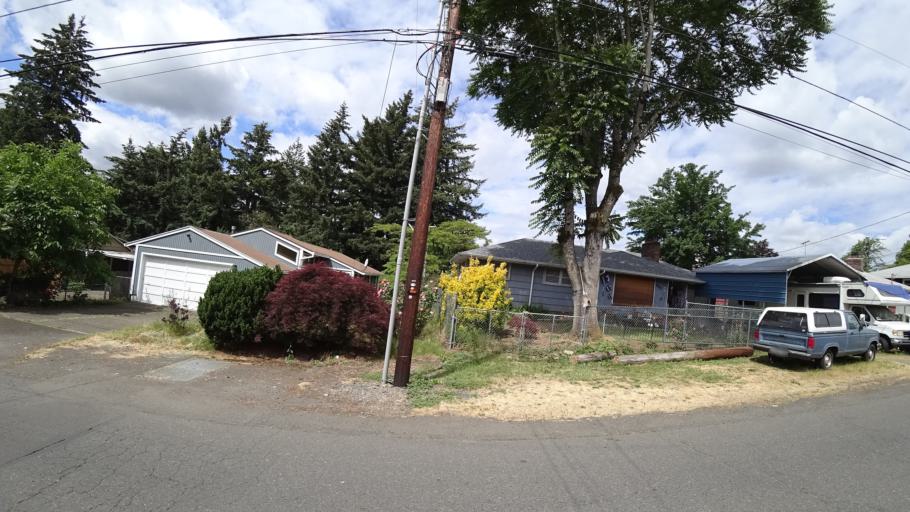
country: US
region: Oregon
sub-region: Multnomah County
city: Lents
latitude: 45.4905
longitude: -122.5300
